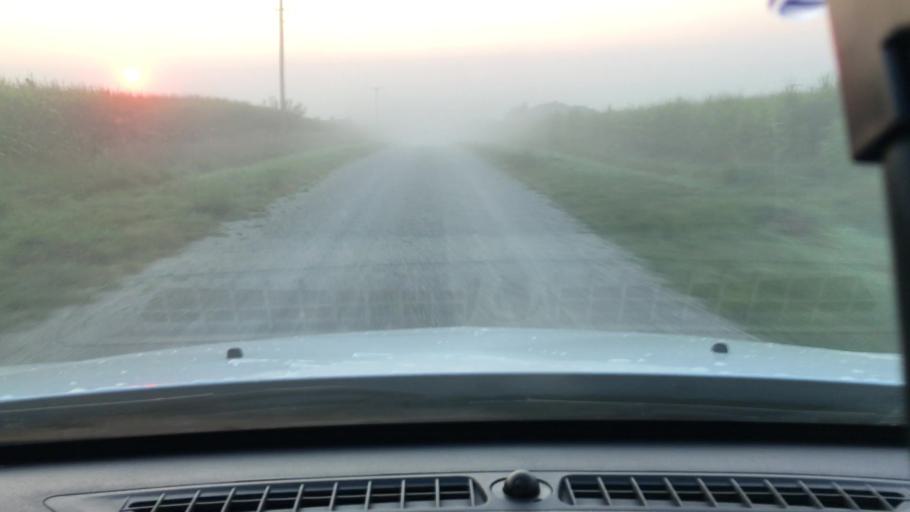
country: US
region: Illinois
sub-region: DeKalb County
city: Malta
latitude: 41.8633
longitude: -88.8404
